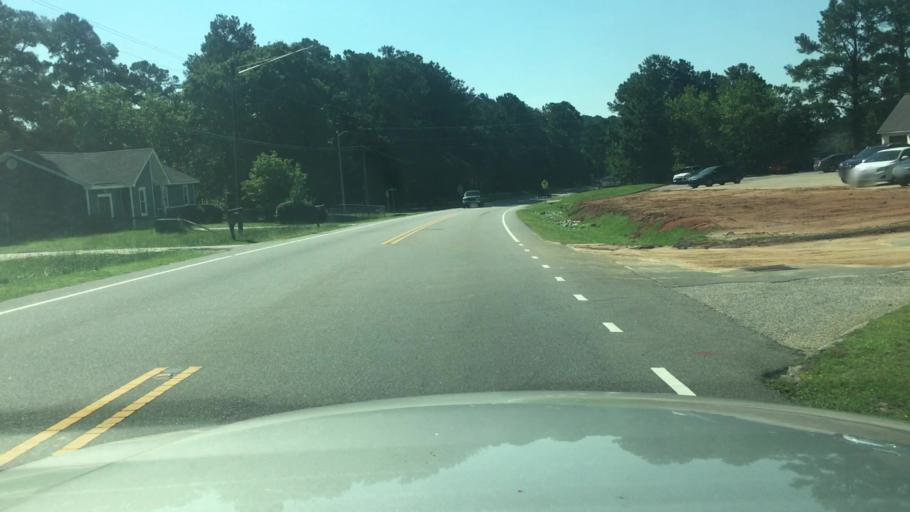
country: US
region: North Carolina
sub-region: Cumberland County
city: Fayetteville
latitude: 35.1119
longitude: -78.9044
